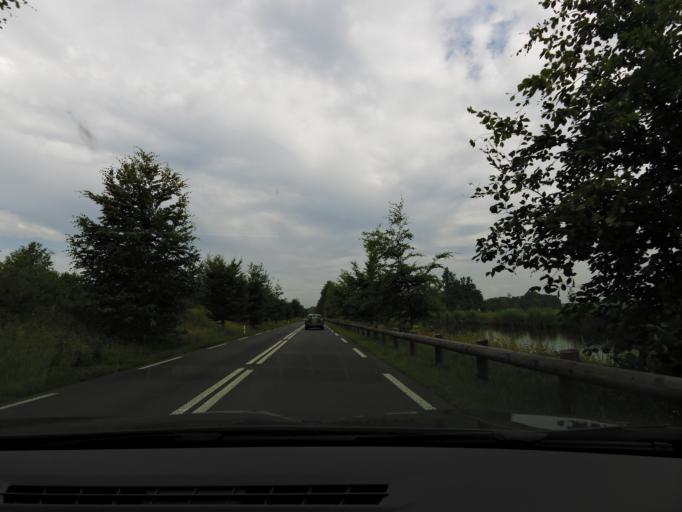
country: NL
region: Gelderland
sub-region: Gemeente Rheden
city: Dieren
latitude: 52.0680
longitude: 6.0936
